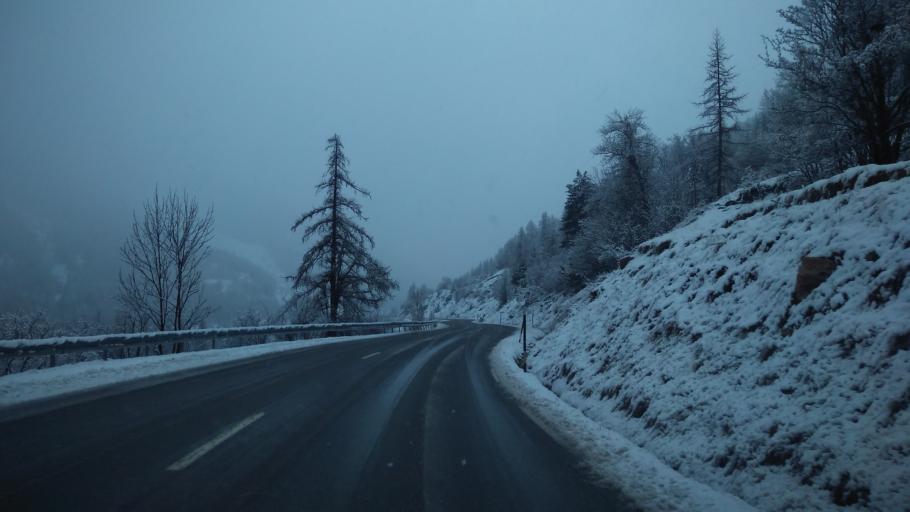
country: FR
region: Provence-Alpes-Cote d'Azur
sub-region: Departement des Hautes-Alpes
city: Le Monetier-les-Bains
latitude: 44.9904
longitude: 6.4862
